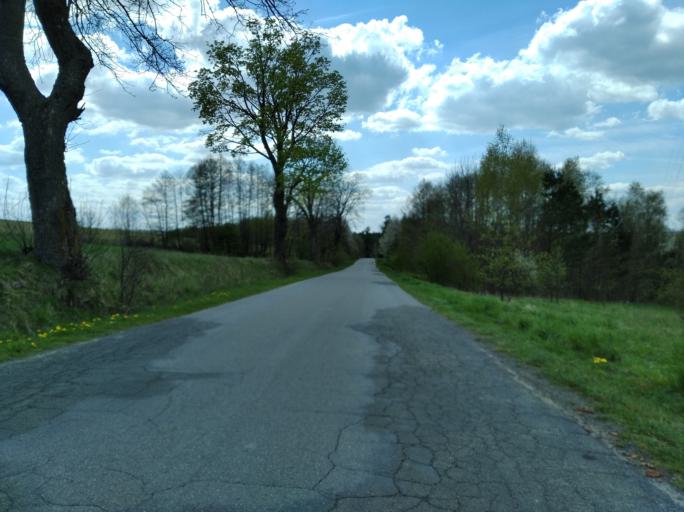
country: PL
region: Subcarpathian Voivodeship
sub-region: Powiat brzozowski
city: Wesola
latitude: 49.7648
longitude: 22.1271
